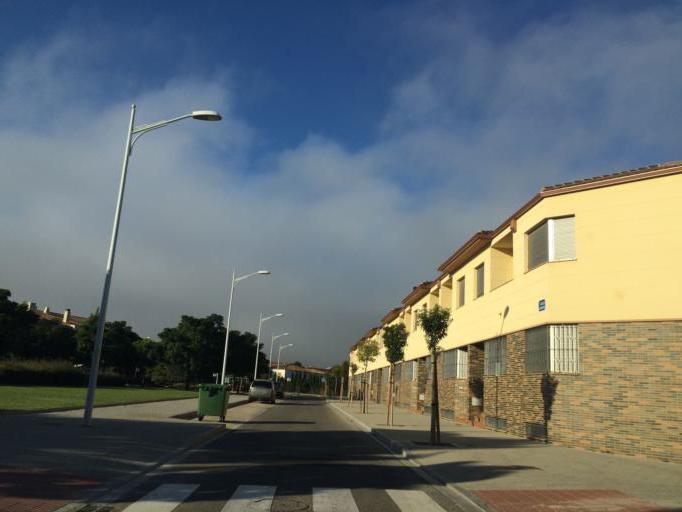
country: ES
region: Castille-La Mancha
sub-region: Provincia de Albacete
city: Albacete
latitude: 39.0045
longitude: -1.8701
